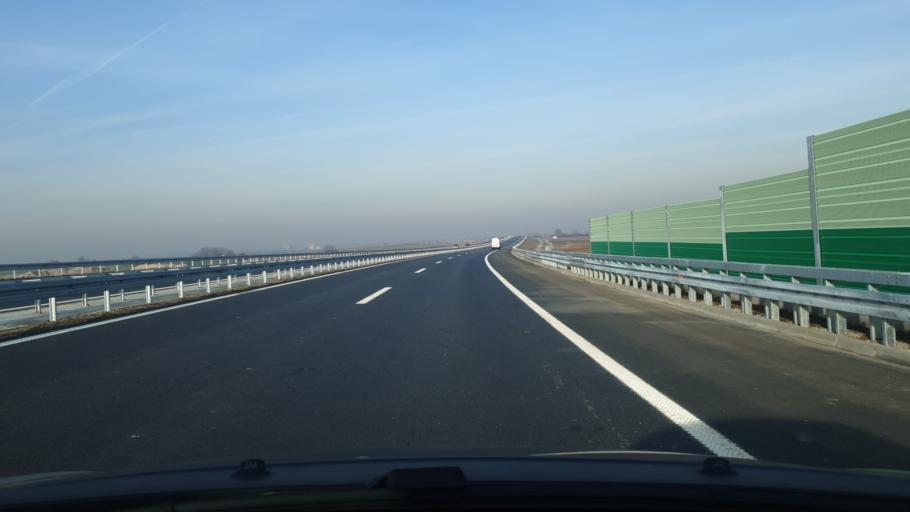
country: RS
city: Boljevci
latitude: 44.7352
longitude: 20.2459
